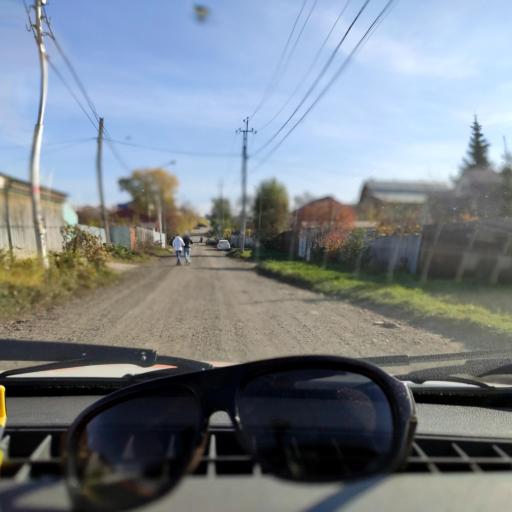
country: RU
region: Bashkortostan
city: Ufa
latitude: 54.7034
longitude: 55.9467
